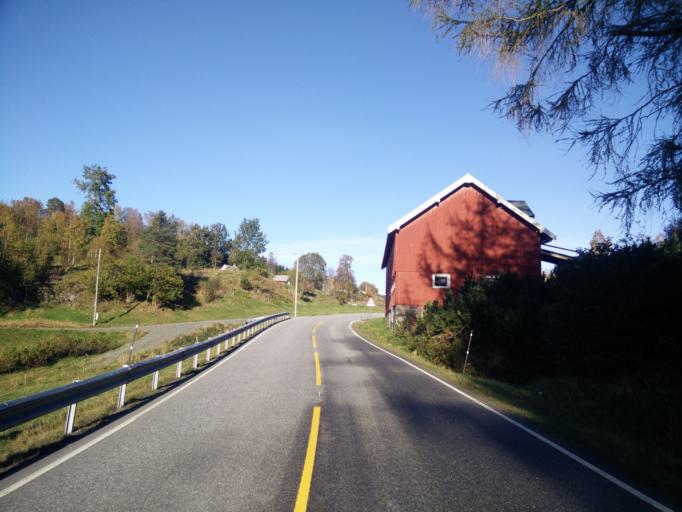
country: NO
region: More og Romsdal
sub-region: Kristiansund
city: Rensvik
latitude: 63.0209
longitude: 8.0136
